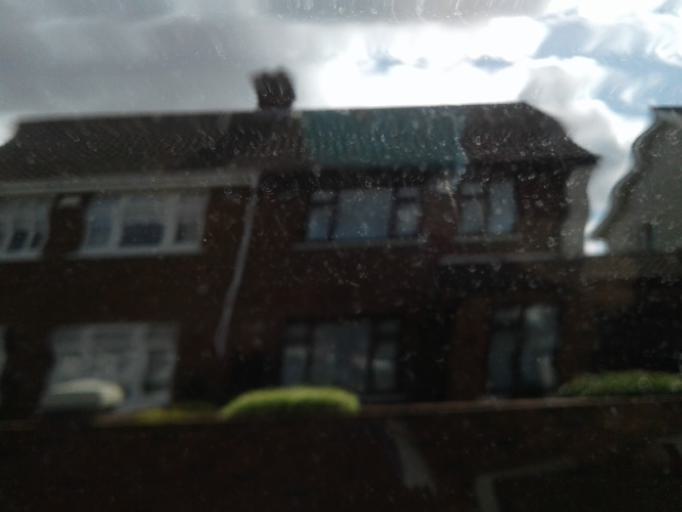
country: IE
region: Leinster
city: Malahide
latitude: 53.4529
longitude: -6.1722
